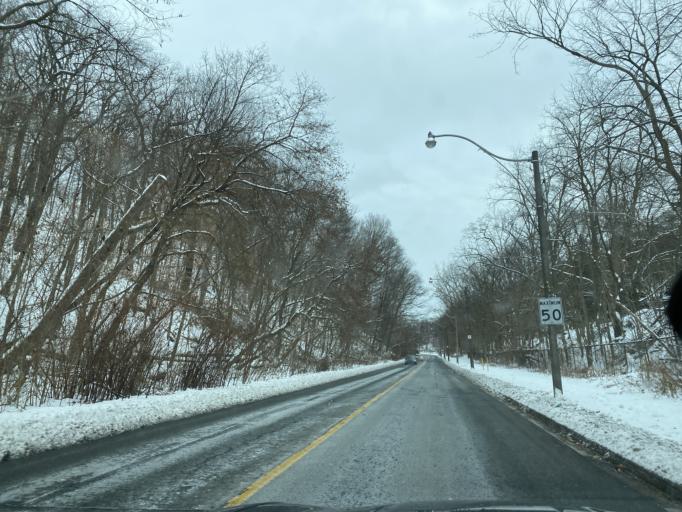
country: CA
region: Ontario
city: Toronto
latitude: 43.6714
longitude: -79.3650
